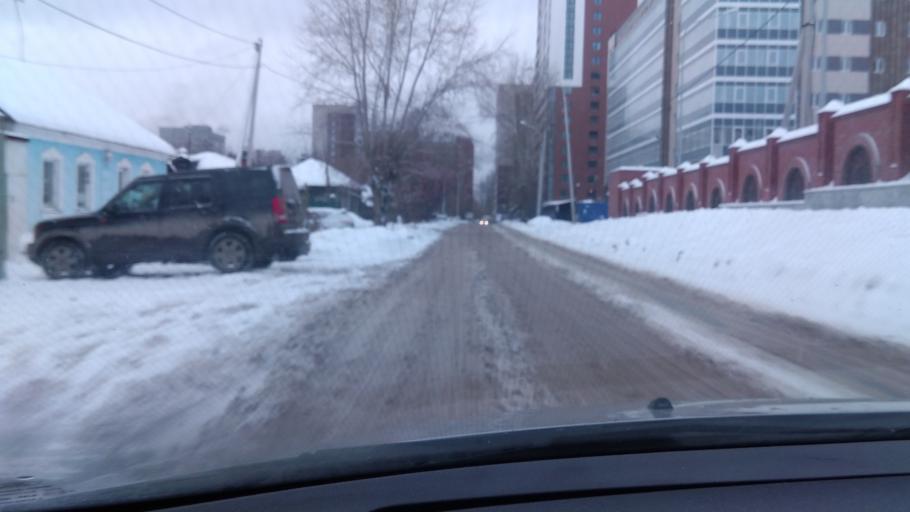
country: RU
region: Sverdlovsk
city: Yekaterinburg
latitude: 56.8046
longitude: 60.5966
